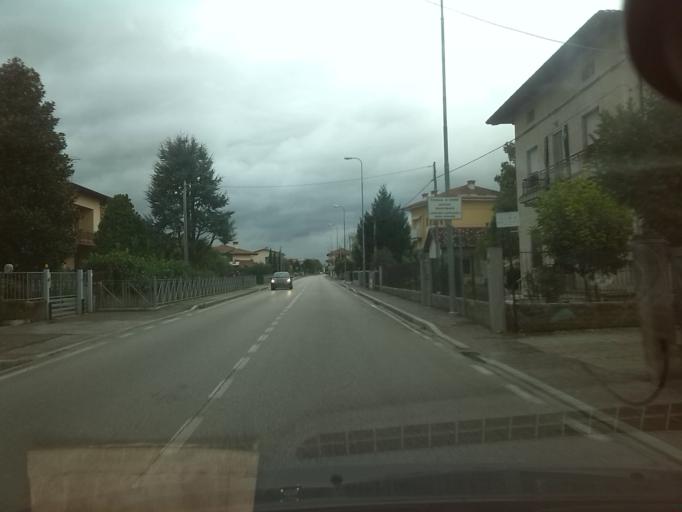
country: IT
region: Friuli Venezia Giulia
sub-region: Provincia di Udine
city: Udine
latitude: 46.0790
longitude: 13.2758
